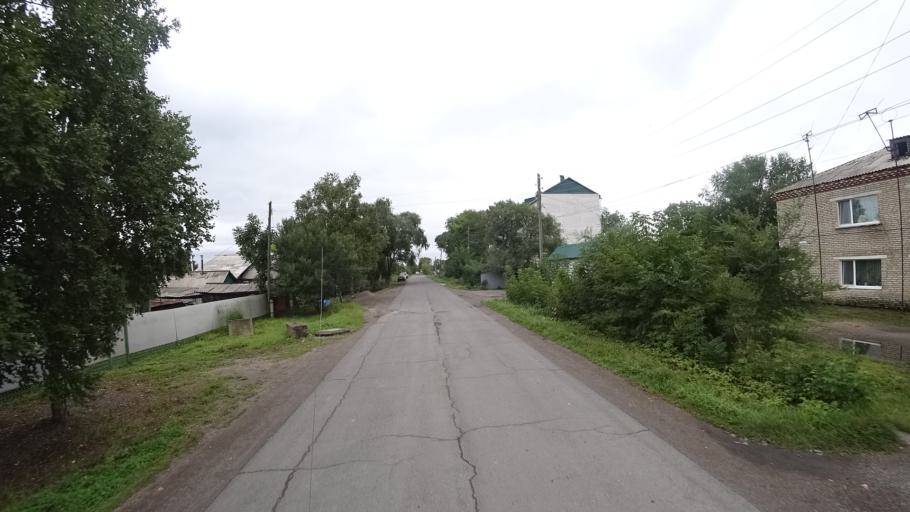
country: RU
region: Primorskiy
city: Chernigovka
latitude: 44.3467
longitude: 132.5703
